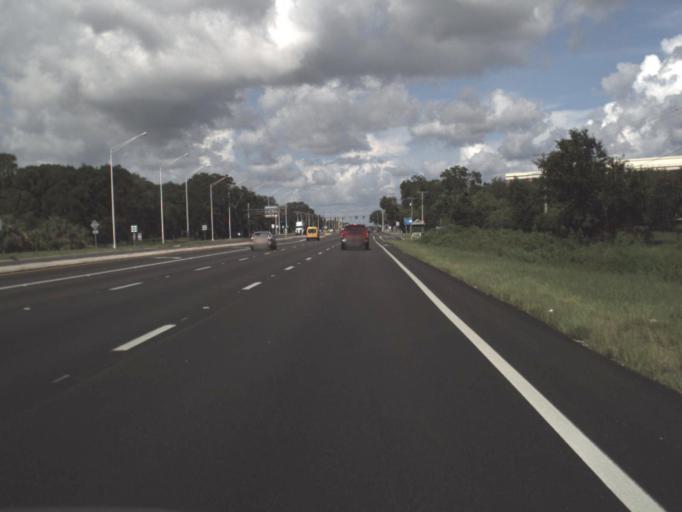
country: US
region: Florida
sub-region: Hillsborough County
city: Mango
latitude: 27.9814
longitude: -82.3305
